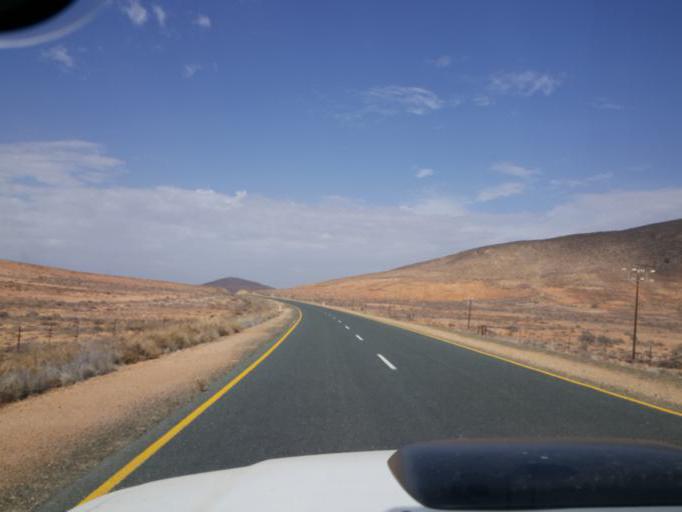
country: ZA
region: Northern Cape
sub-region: Namakwa District Municipality
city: Springbok
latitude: -29.2597
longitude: 17.5083
